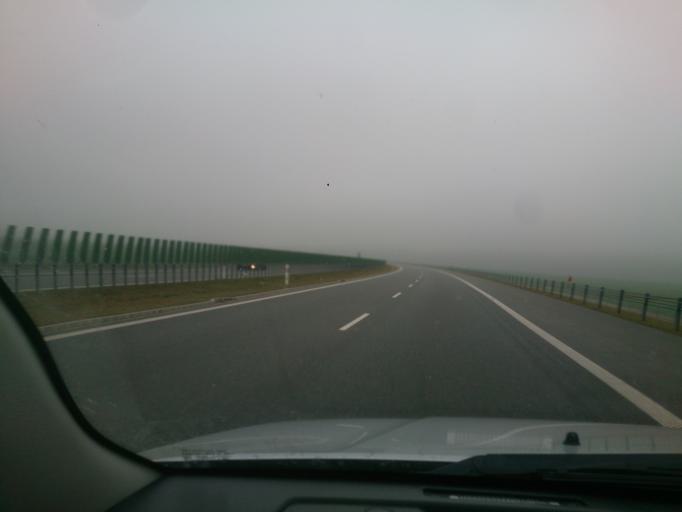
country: PL
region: Kujawsko-Pomorskie
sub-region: Grudziadz
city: Grudziadz
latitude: 53.4533
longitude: 18.6622
